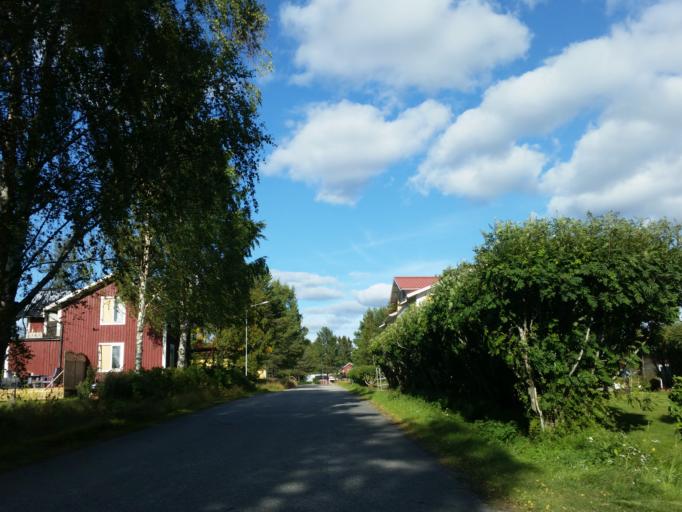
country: SE
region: Vaesterbotten
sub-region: Robertsfors Kommun
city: Robertsfors
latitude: 64.1695
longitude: 20.9373
